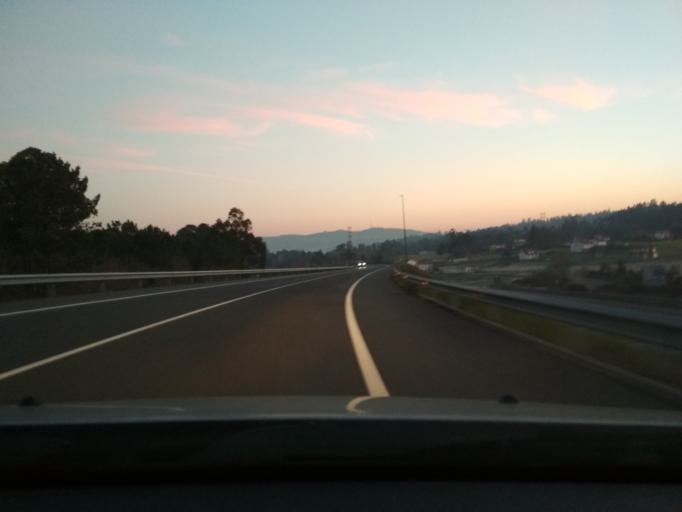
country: ES
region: Galicia
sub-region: Provincia da Coruna
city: Santiago de Compostela
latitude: 42.8438
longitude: -8.5947
